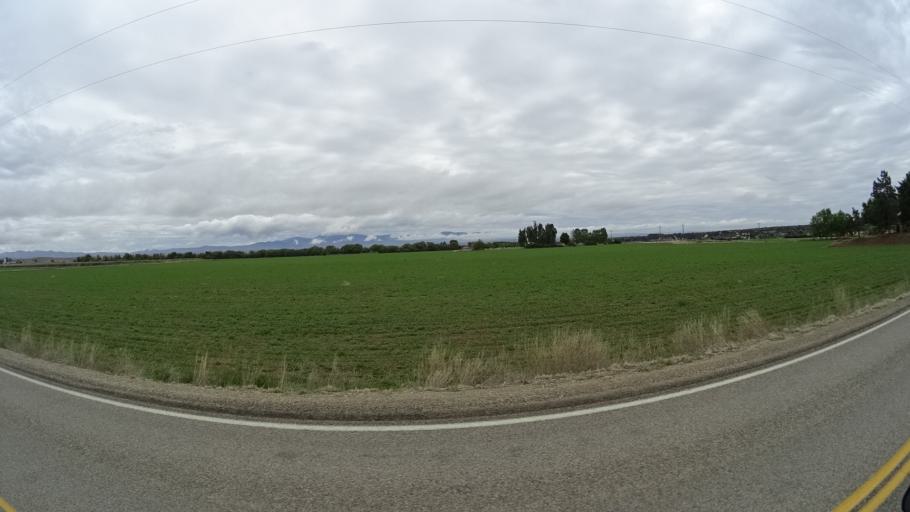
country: US
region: Idaho
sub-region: Ada County
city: Star
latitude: 43.7093
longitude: -116.4437
